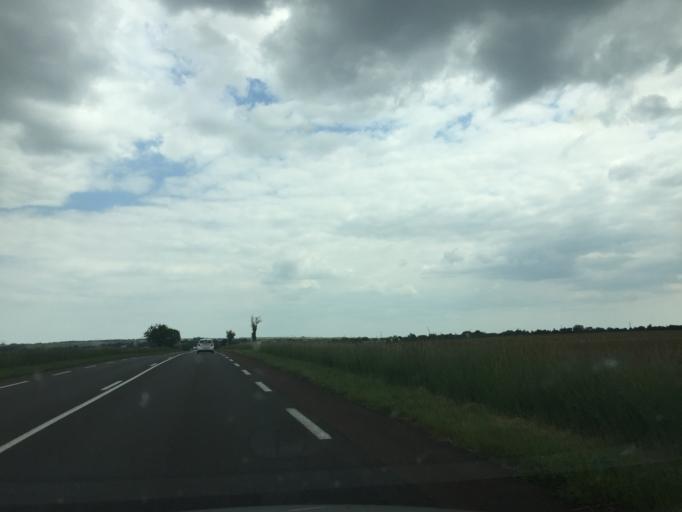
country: FR
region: Pays de la Loire
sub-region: Departement de la Vendee
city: Benet
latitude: 46.3803
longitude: -0.6052
